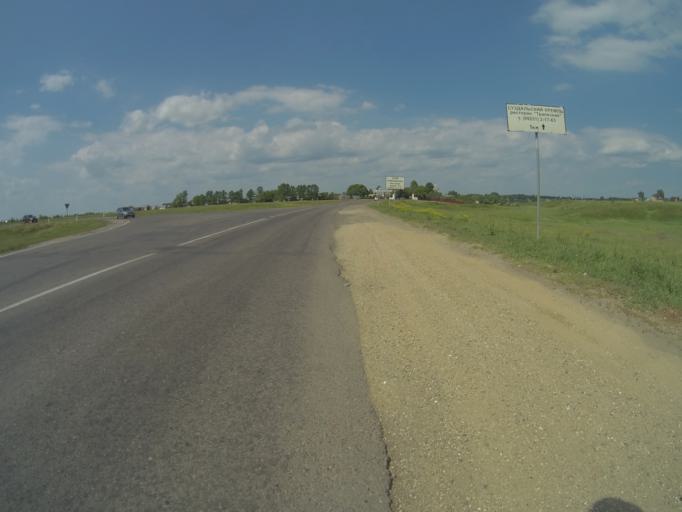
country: RU
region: Vladimir
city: Suzdal'
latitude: 56.4038
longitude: 40.4454
